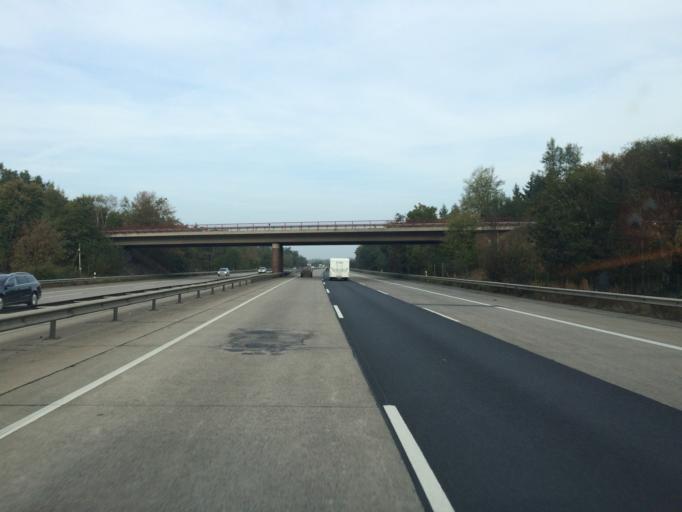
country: DE
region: Lower Saxony
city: Elze
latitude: 52.5880
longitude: 9.7595
